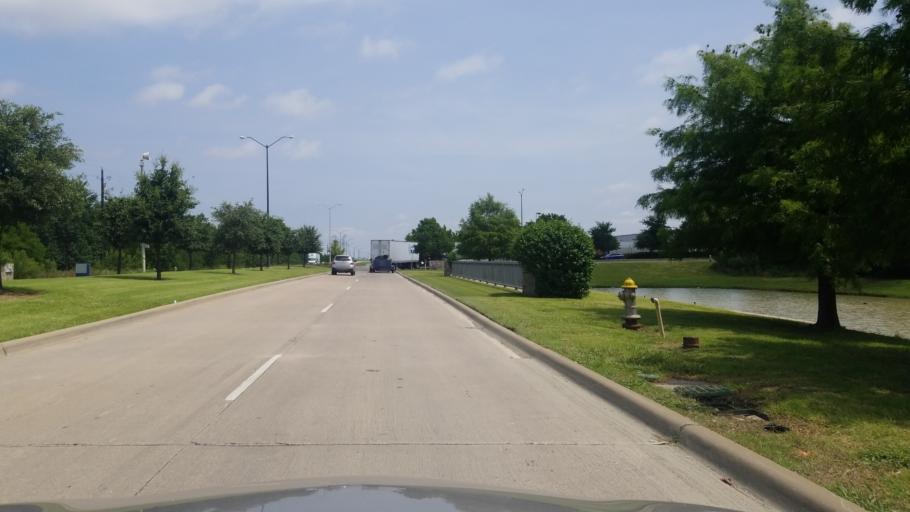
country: US
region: Texas
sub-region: Dallas County
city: Duncanville
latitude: 32.6887
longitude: -96.9630
